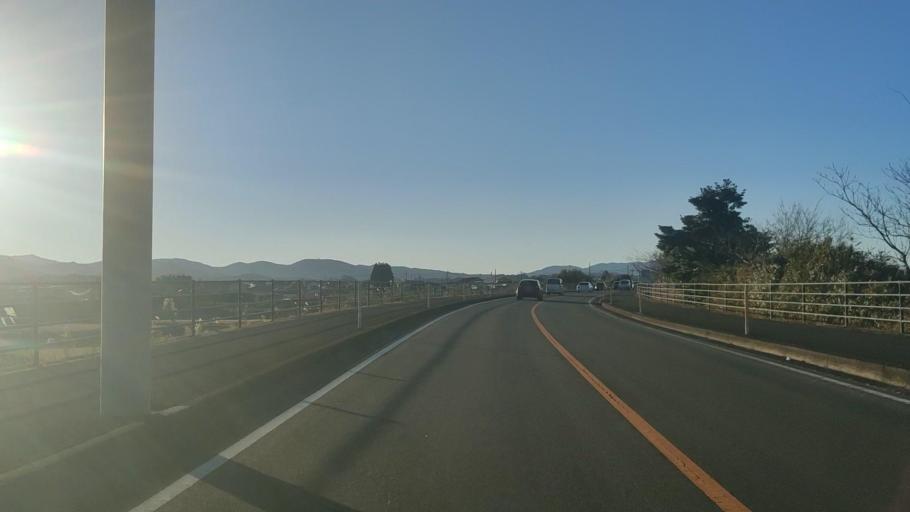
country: JP
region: Miyazaki
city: Miyazaki-shi
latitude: 31.8312
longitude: 131.3040
